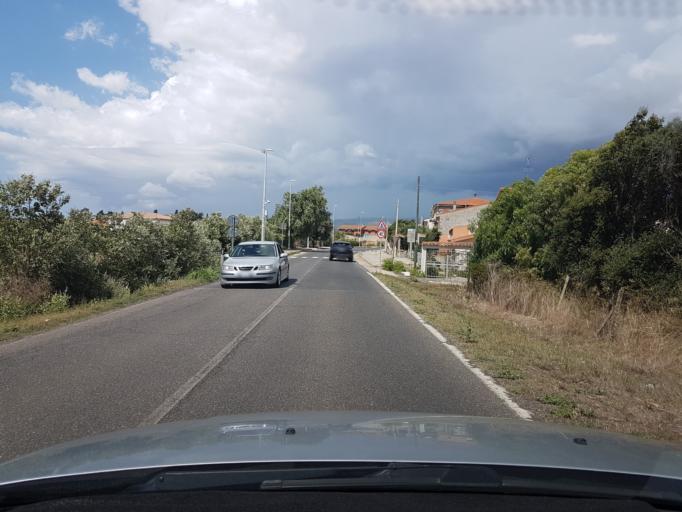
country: IT
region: Sardinia
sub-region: Provincia di Oristano
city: Riola Sardo
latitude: 39.9875
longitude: 8.5407
